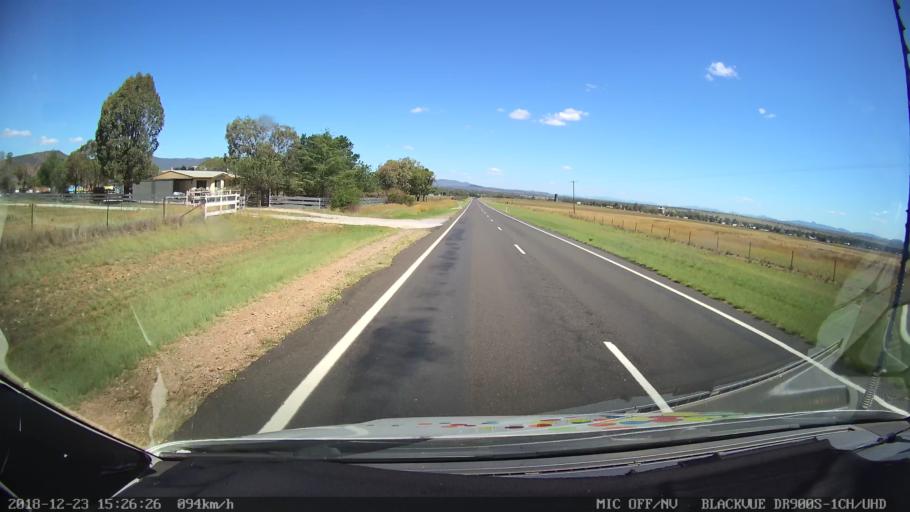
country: AU
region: New South Wales
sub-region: Tamworth Municipality
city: East Tamworth
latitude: -30.9168
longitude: 150.8383
